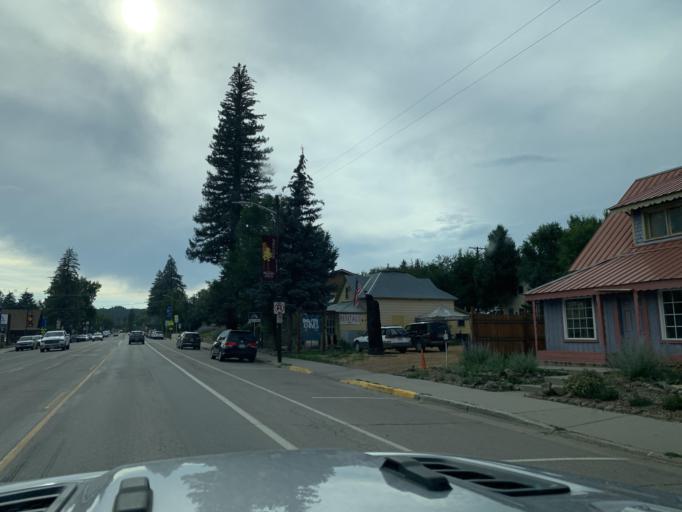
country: US
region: Colorado
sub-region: Archuleta County
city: Pagosa Springs
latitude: 37.2690
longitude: -107.0039
